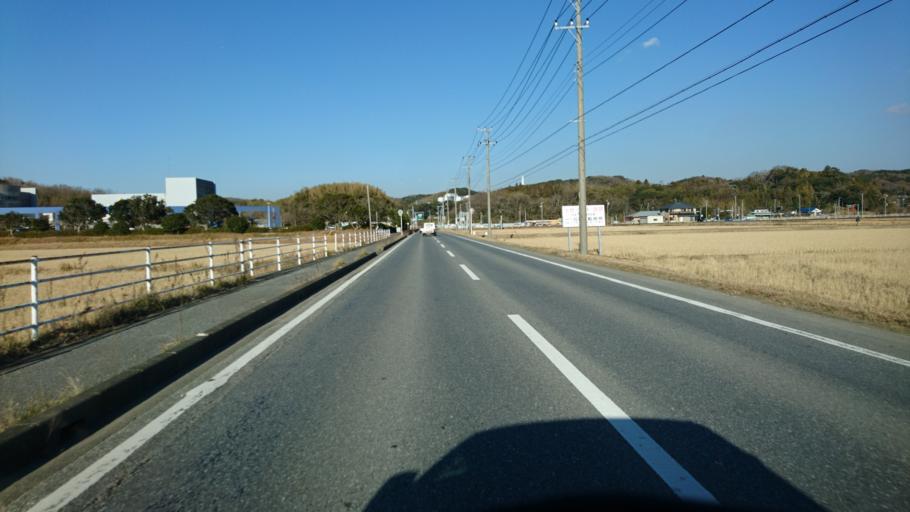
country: JP
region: Chiba
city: Kimitsu
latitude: 35.3152
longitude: 139.9351
